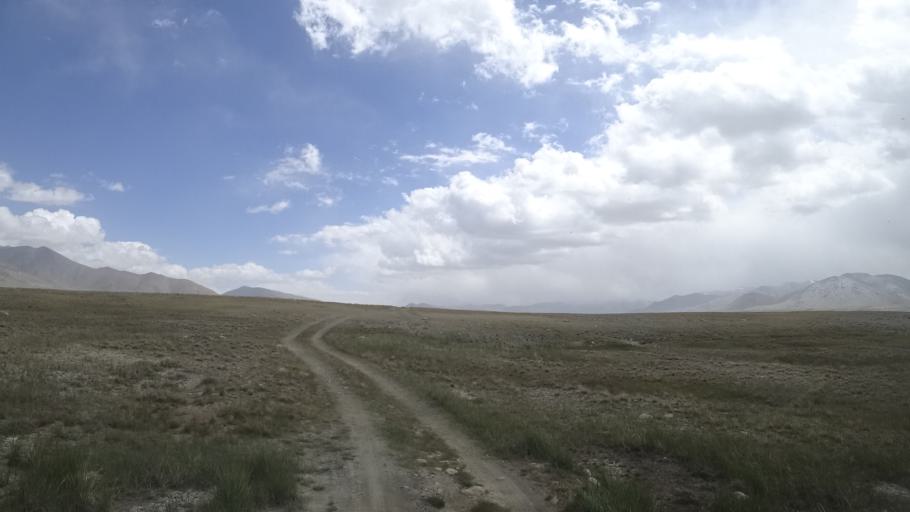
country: TJ
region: Gorno-Badakhshan
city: Murghob
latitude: 37.4721
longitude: 73.9639
